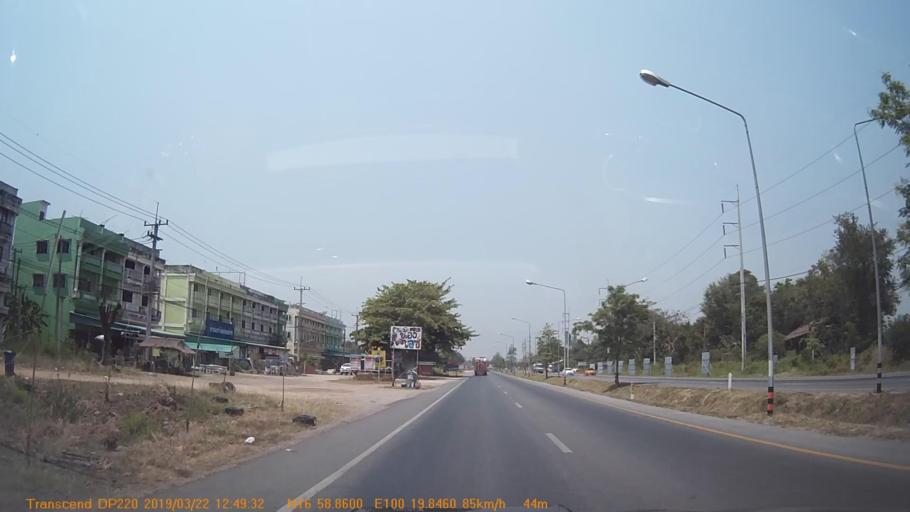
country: TH
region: Phitsanulok
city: Wat Bot
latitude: 16.9813
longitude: 100.3306
